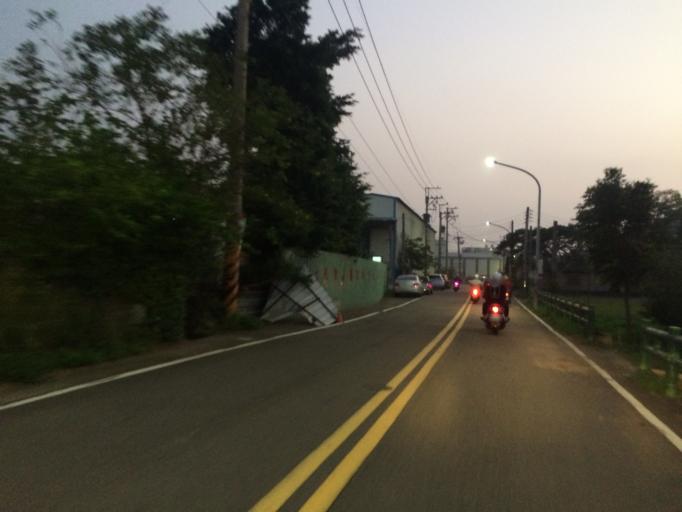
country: TW
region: Taiwan
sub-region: Hsinchu
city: Hsinchu
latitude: 24.7759
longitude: 120.9172
